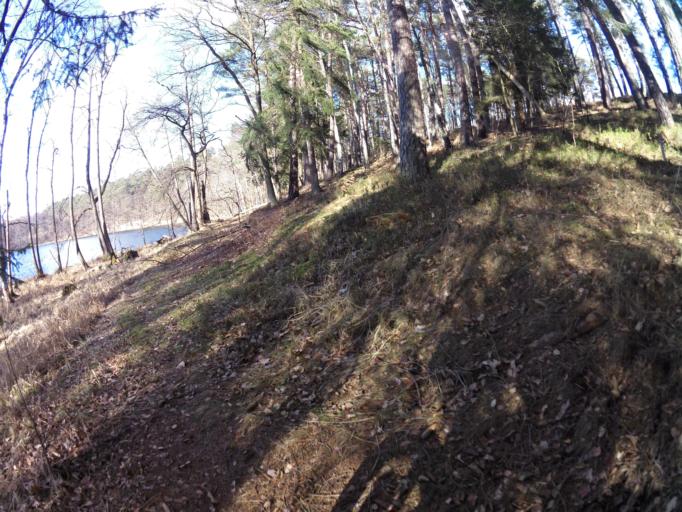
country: PL
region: West Pomeranian Voivodeship
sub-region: Powiat mysliborski
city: Debno
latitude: 52.7754
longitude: 14.7362
